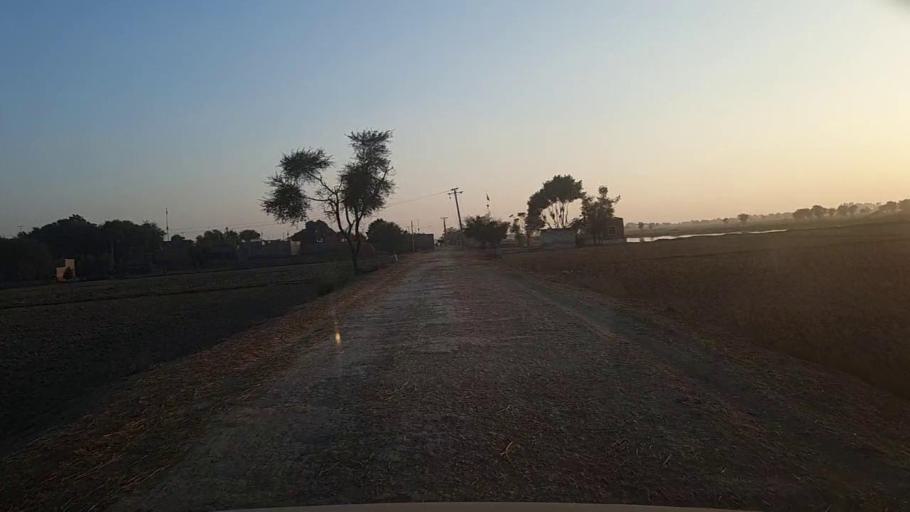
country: PK
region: Sindh
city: Khairpur Nathan Shah
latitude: 27.1715
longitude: 67.7330
